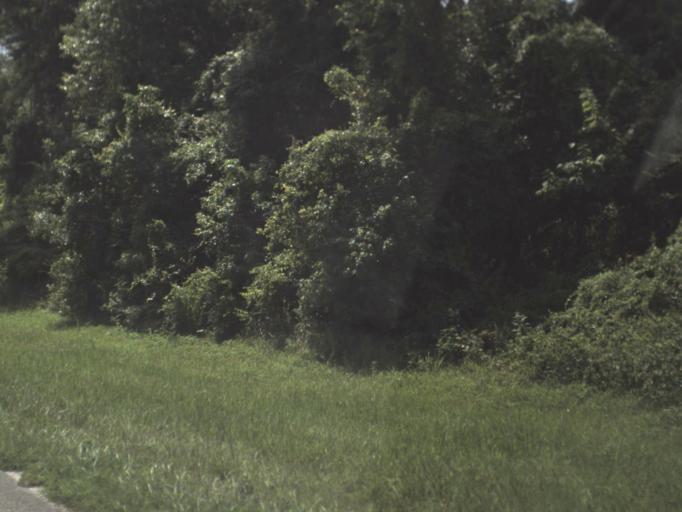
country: US
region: Florida
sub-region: Hernando County
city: Ridge Manor
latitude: 28.5077
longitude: -82.1433
